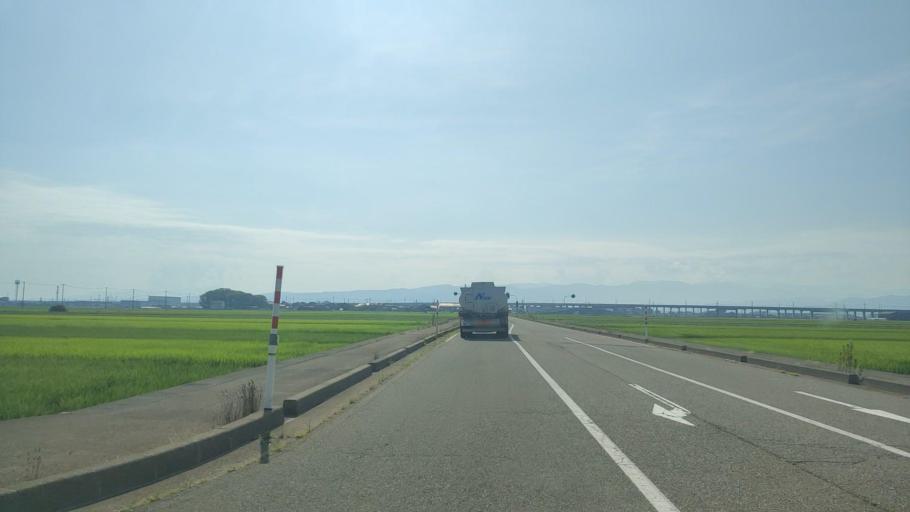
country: JP
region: Ishikawa
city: Matsuto
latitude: 36.5000
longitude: 136.5079
